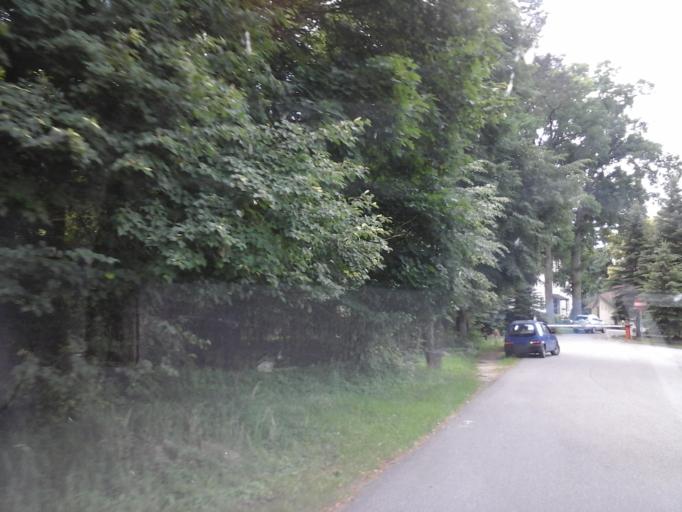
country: PL
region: West Pomeranian Voivodeship
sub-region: Powiat goleniowski
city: Goleniow
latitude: 53.4568
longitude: 14.7905
